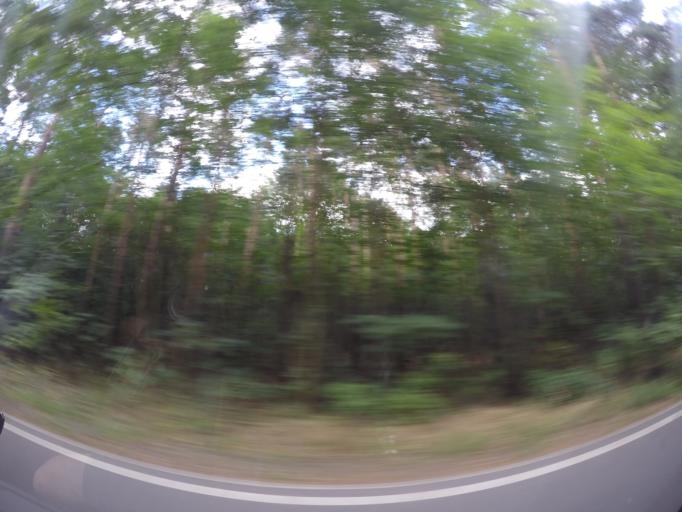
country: DE
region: Berlin
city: Kopenick Bezirk
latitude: 52.4574
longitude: 13.5624
